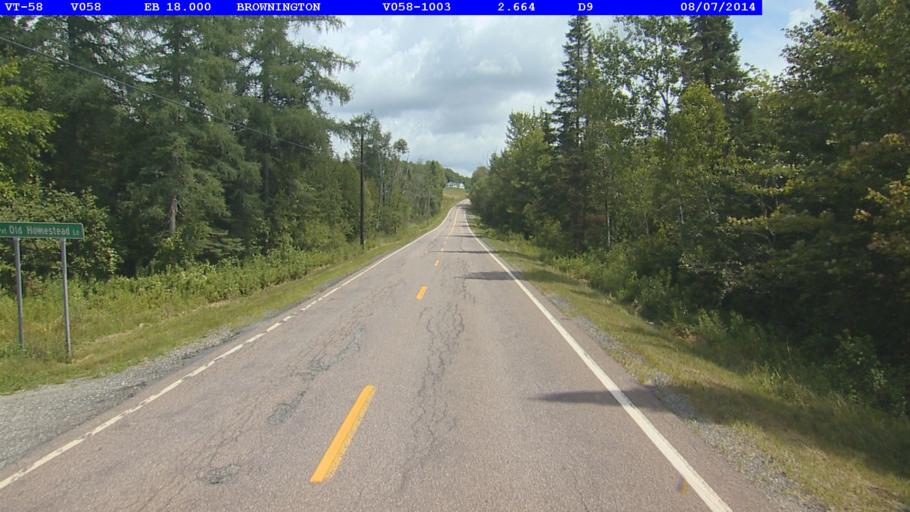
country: US
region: Vermont
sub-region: Orleans County
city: Newport
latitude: 44.7951
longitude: -72.0953
